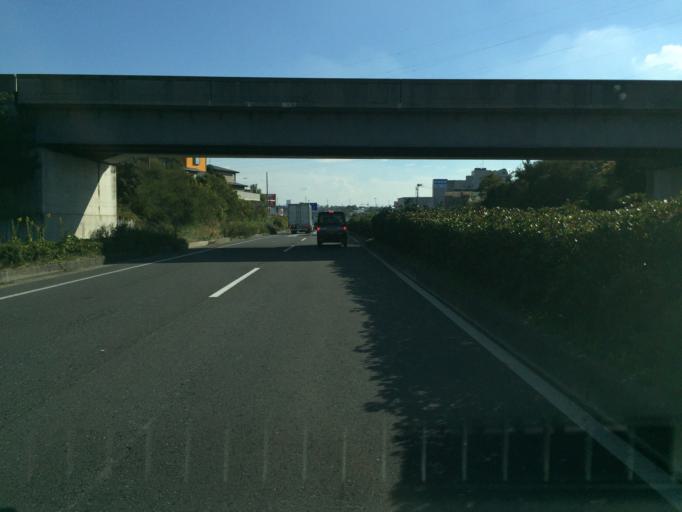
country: JP
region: Fukushima
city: Koriyama
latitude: 37.4521
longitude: 140.3788
